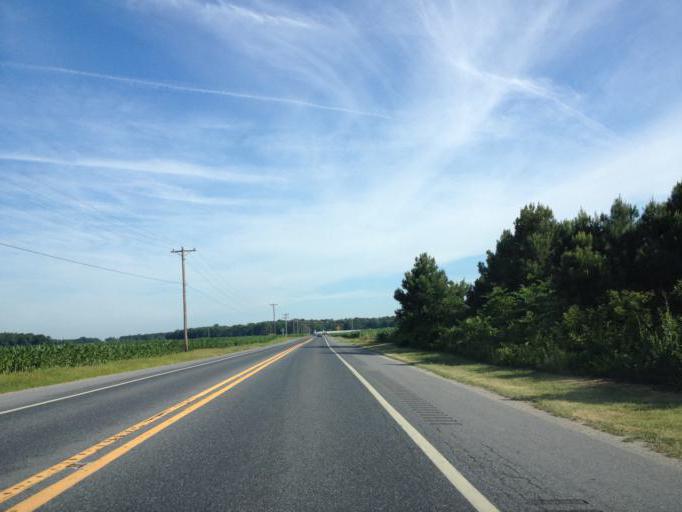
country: US
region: Delaware
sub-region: Sussex County
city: Selbyville
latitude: 38.5159
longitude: -75.1842
